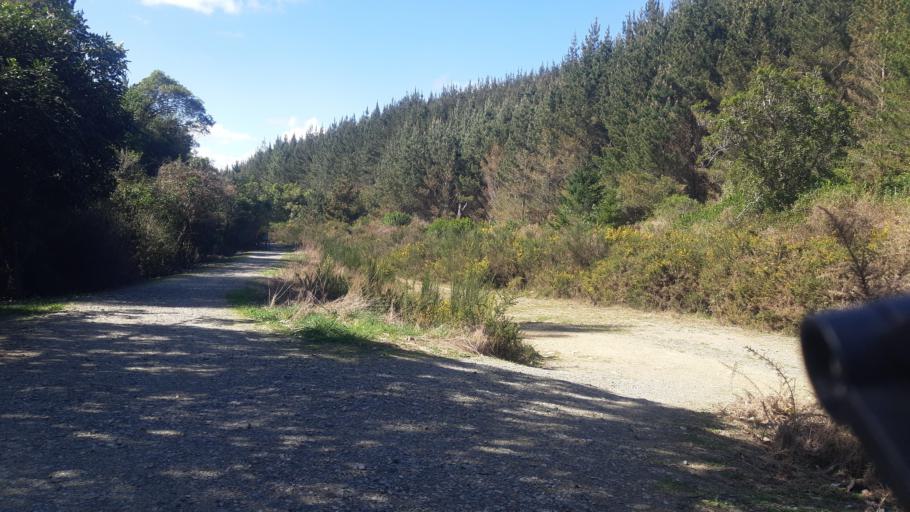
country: NZ
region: Tasman
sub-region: Tasman District
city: Wakefield
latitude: -41.4885
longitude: 172.9160
